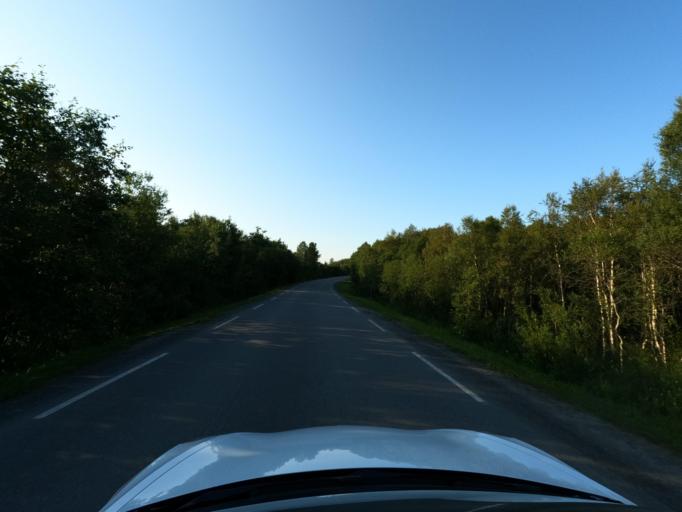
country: NO
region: Troms
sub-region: Skanland
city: Evenskjer
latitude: 68.4851
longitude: 16.7117
